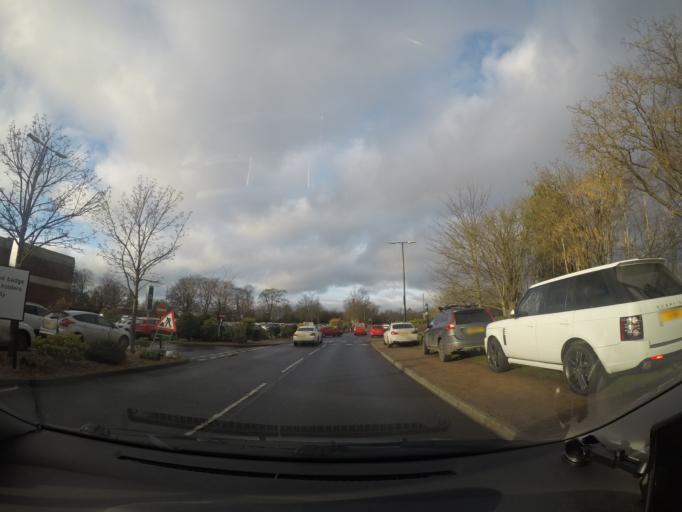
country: GB
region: England
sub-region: City of York
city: Fulford
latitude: 53.9236
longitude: -1.0771
